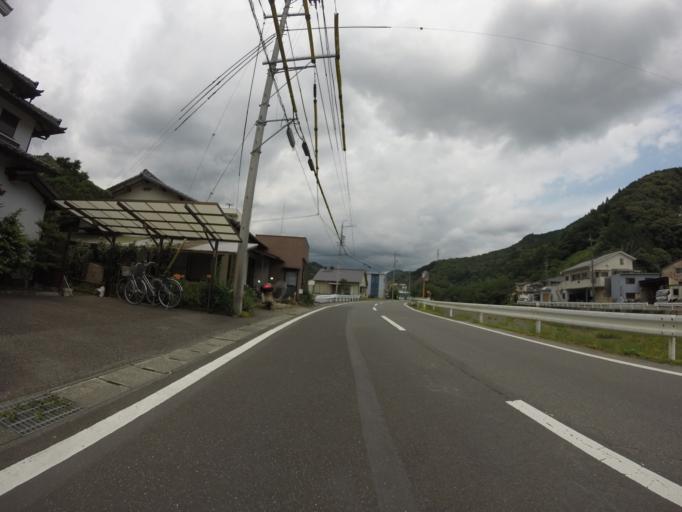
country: JP
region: Shizuoka
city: Shizuoka-shi
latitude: 34.9904
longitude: 138.3066
